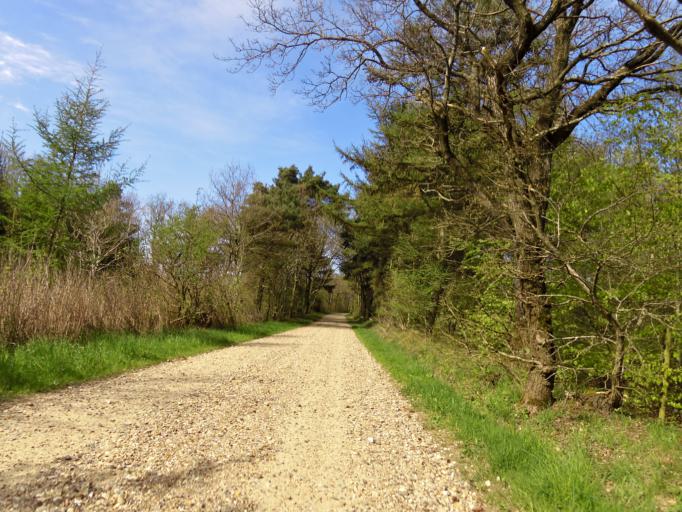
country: DK
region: Central Jutland
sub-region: Holstebro Kommune
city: Vinderup
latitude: 56.4814
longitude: 8.8713
